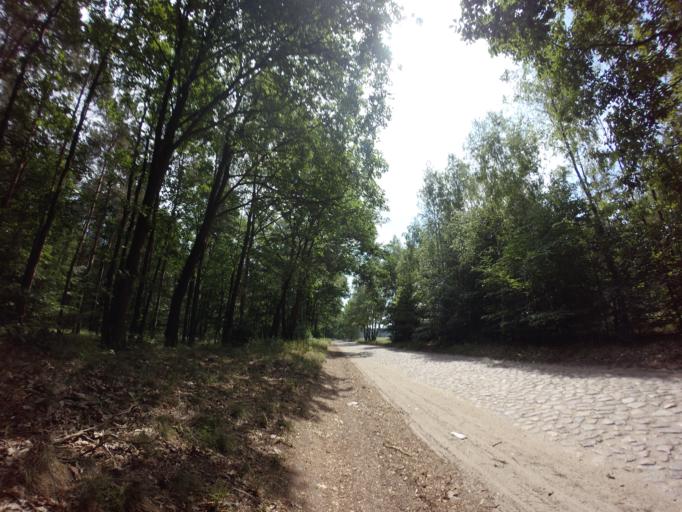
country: PL
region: Lubusz
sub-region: Powiat strzelecko-drezdenecki
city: Dobiegniew
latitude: 53.0897
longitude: 15.7991
